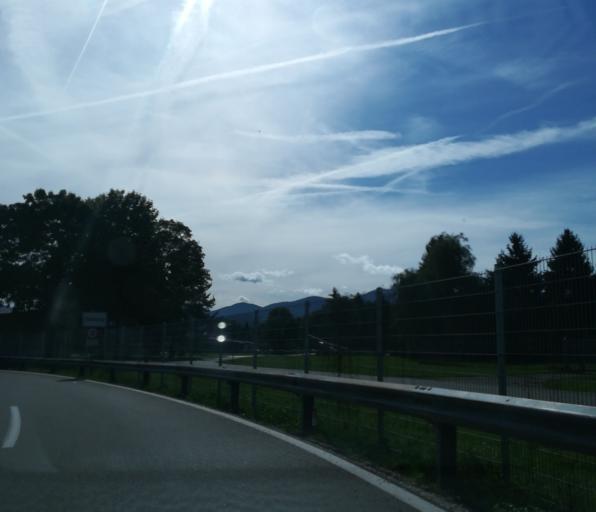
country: AT
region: Styria
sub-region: Politischer Bezirk Murtal
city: Flatschach
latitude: 47.2018
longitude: 14.7613
